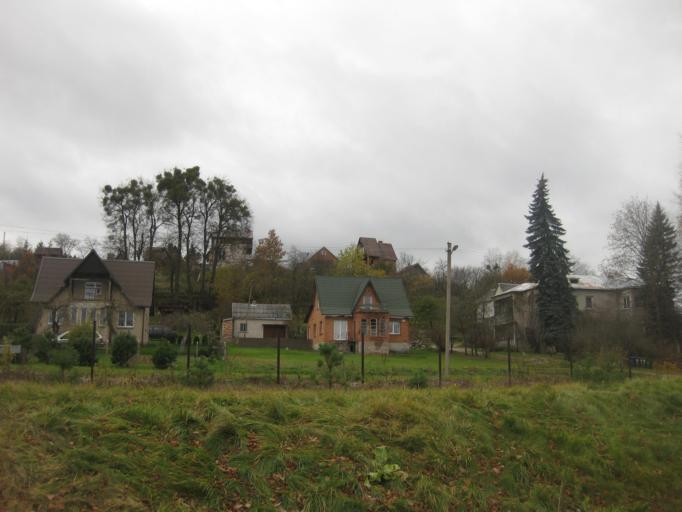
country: LT
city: Prienai
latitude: 54.6357
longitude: 23.9429
